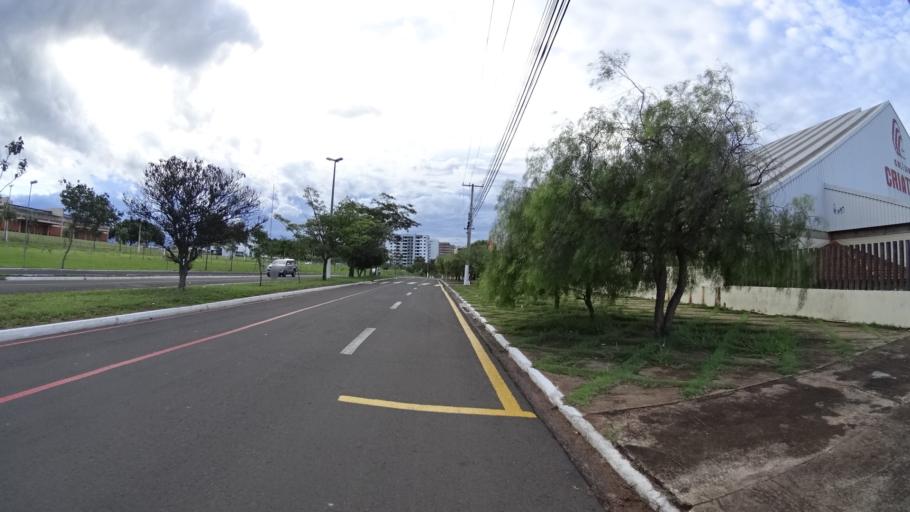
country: BR
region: Sao Paulo
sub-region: Marilia
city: Marilia
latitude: -22.2285
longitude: -49.9250
